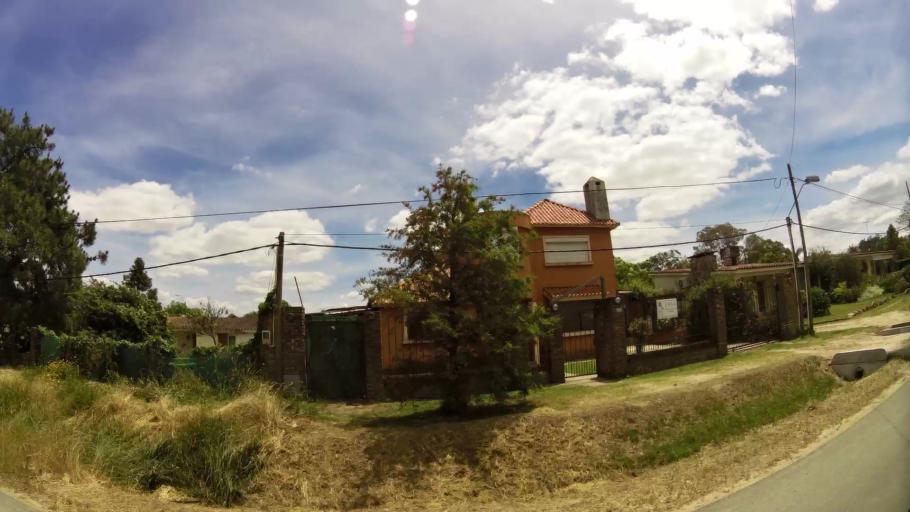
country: UY
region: Canelones
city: Colonia Nicolich
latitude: -34.8258
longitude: -55.9696
